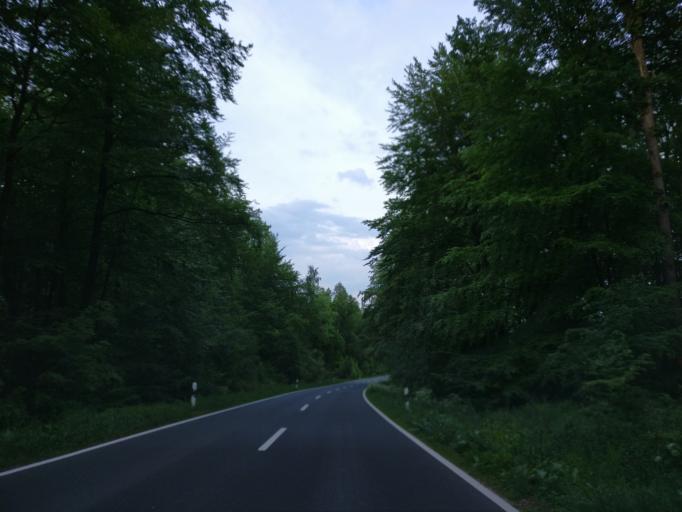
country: DE
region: Lower Saxony
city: Hannoversch Munden
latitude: 51.4033
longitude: 9.6963
